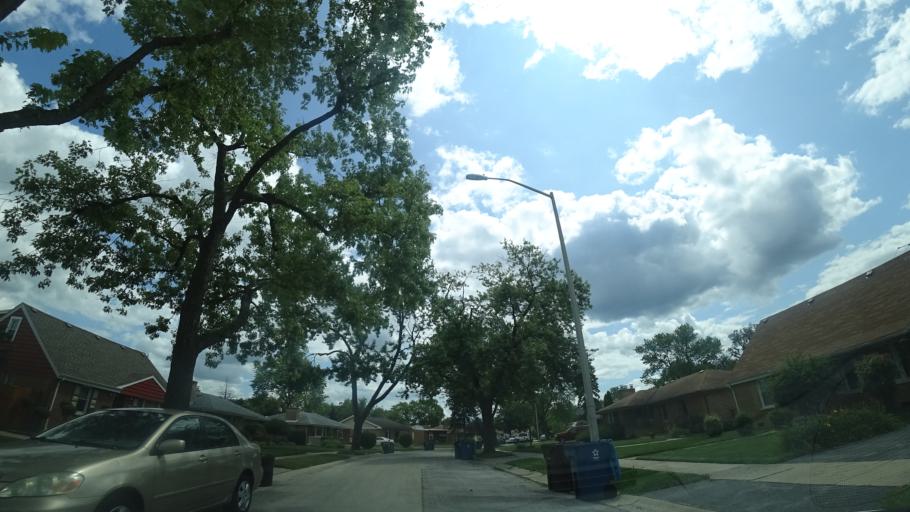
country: US
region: Illinois
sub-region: Cook County
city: Alsip
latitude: 41.6820
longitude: -87.7313
